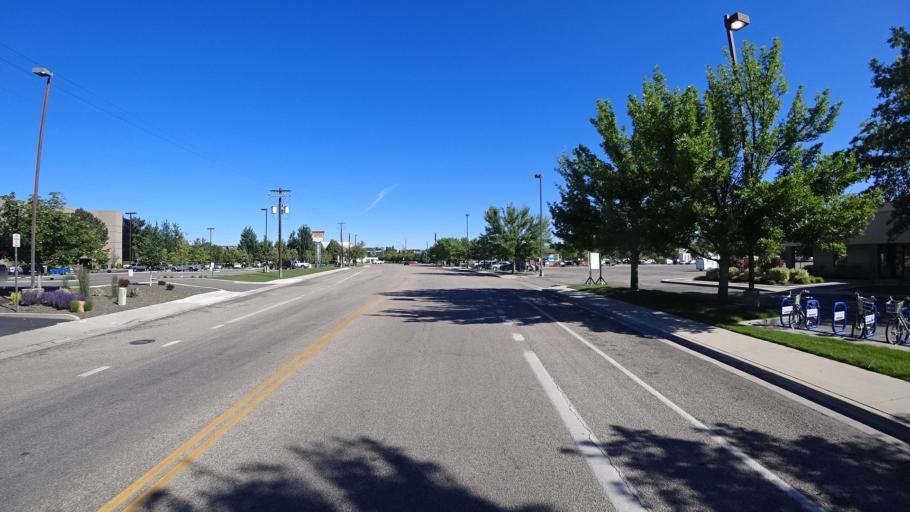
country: US
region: Idaho
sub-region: Ada County
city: Boise
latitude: 43.6154
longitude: -116.2192
